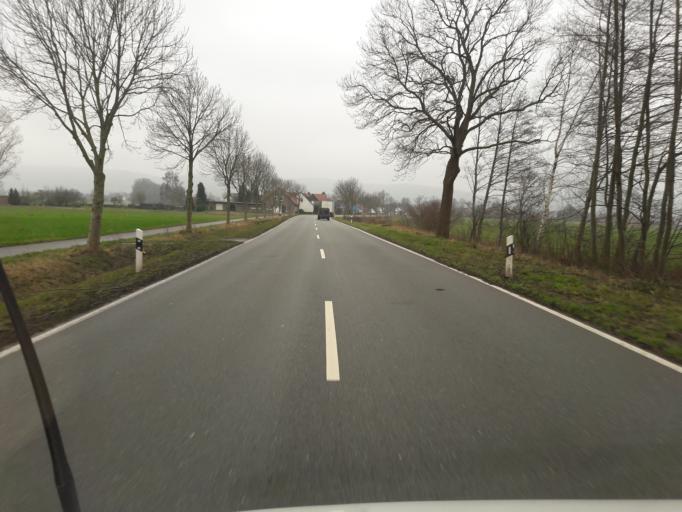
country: DE
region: North Rhine-Westphalia
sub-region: Regierungsbezirk Detmold
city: Hille
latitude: 52.2957
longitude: 8.8013
